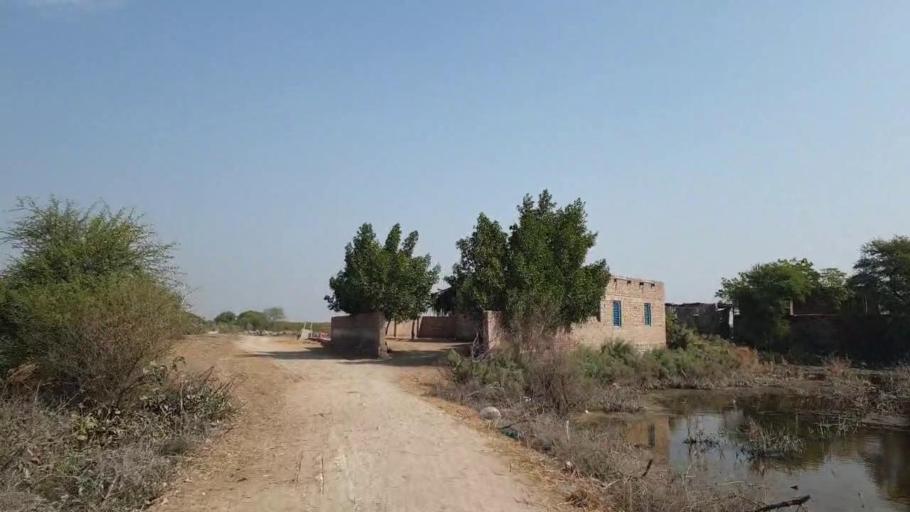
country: PK
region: Sindh
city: Tando Muhammad Khan
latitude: 25.0788
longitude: 68.4221
